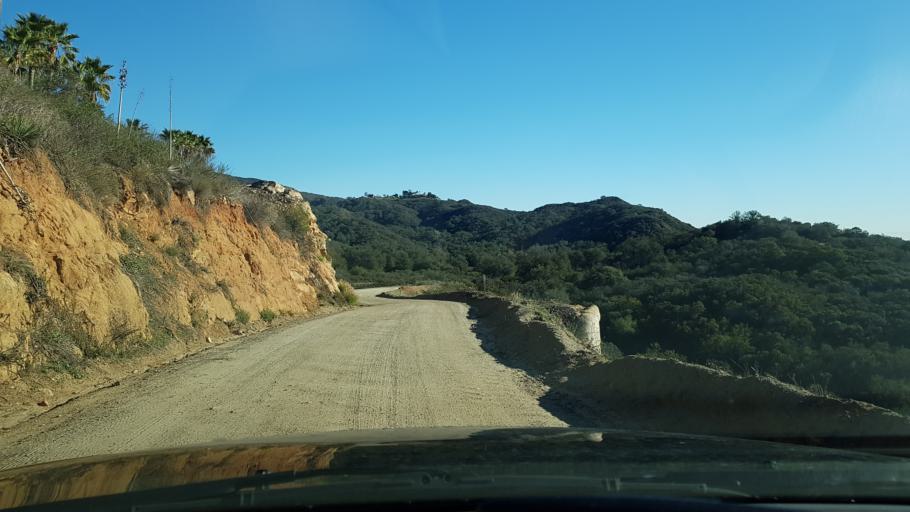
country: US
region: California
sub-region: San Diego County
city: Hidden Meadows
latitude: 33.2118
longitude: -117.0872
